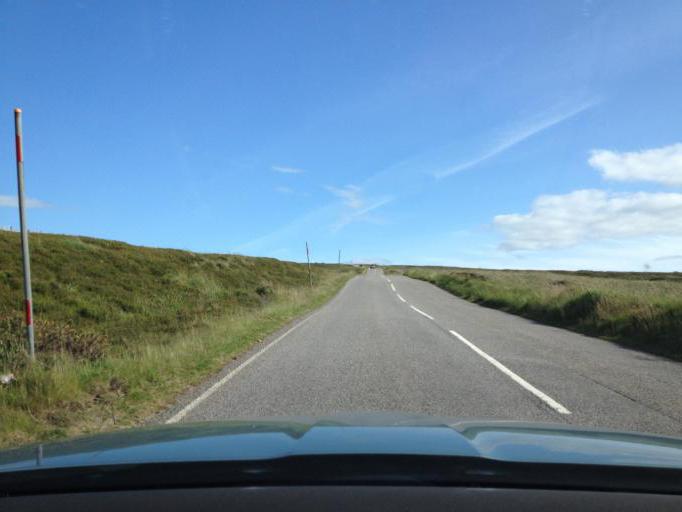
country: GB
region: Scotland
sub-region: Aberdeenshire
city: Laurencekirk
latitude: 56.9216
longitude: -2.5801
